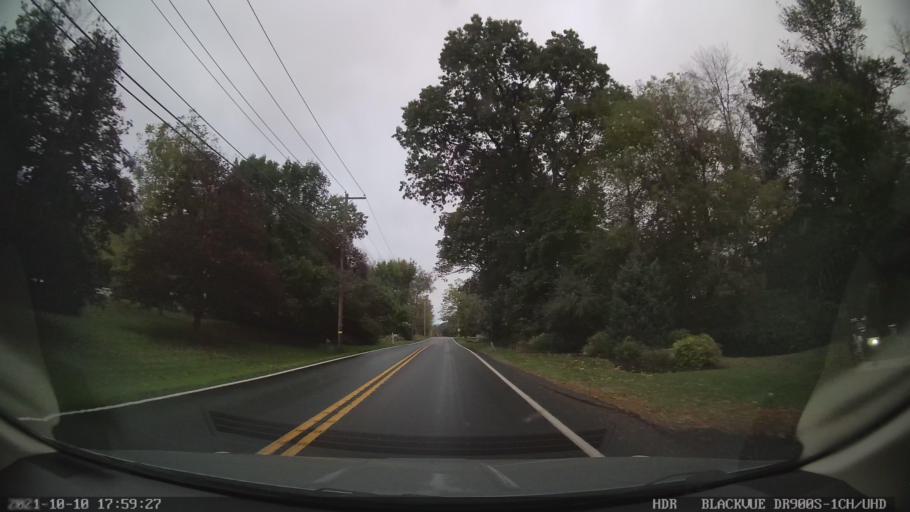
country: US
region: Pennsylvania
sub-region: Lehigh County
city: Egypt
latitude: 40.6376
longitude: -75.5593
